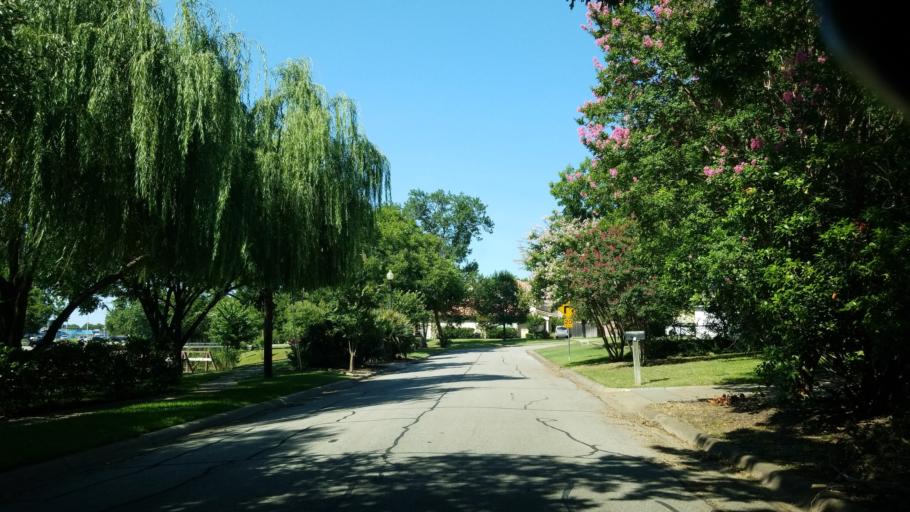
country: US
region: Texas
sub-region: Dallas County
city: Farmers Branch
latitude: 32.9224
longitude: -96.8900
